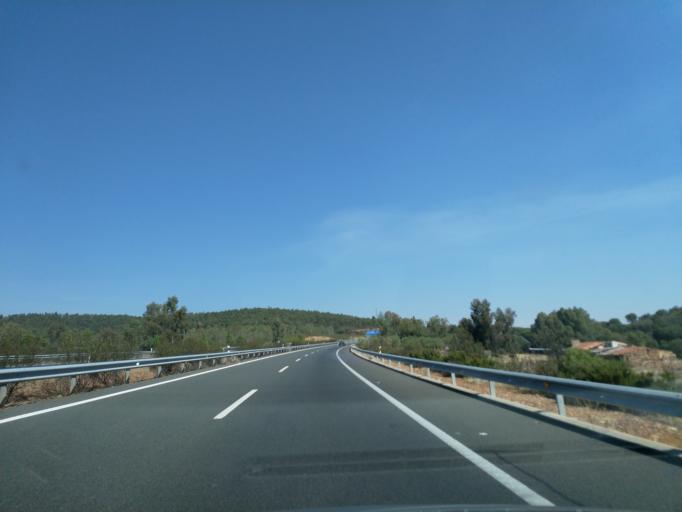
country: ES
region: Extremadura
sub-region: Provincia de Caceres
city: Alcuescar
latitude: 39.1501
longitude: -6.2750
